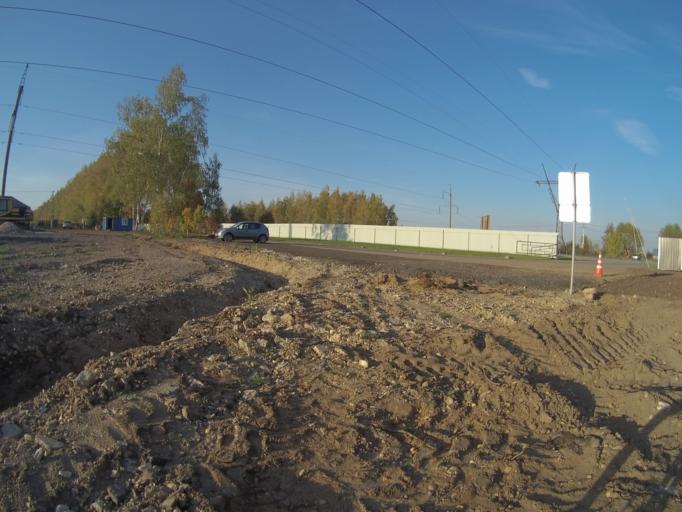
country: RU
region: Vladimir
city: Vladimir
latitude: 56.1749
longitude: 40.3334
